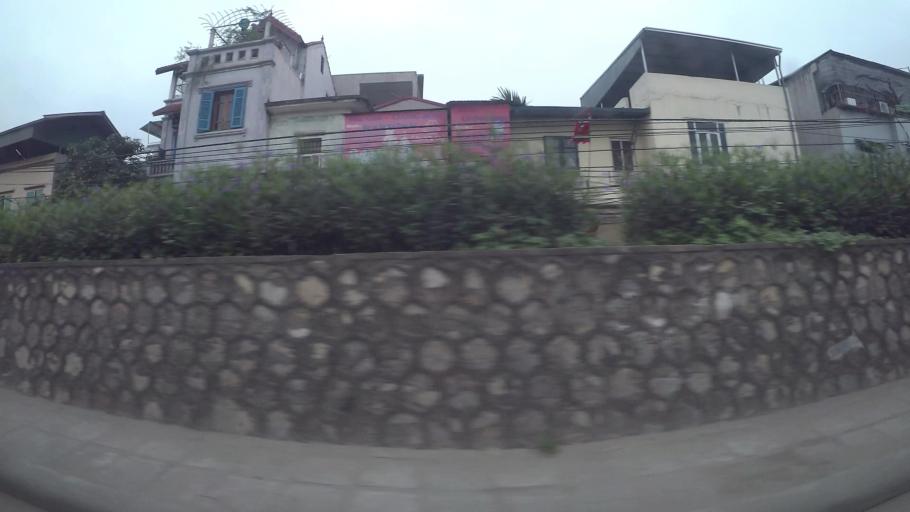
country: VN
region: Ha Noi
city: Hai BaTrung
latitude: 21.0001
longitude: 105.8856
